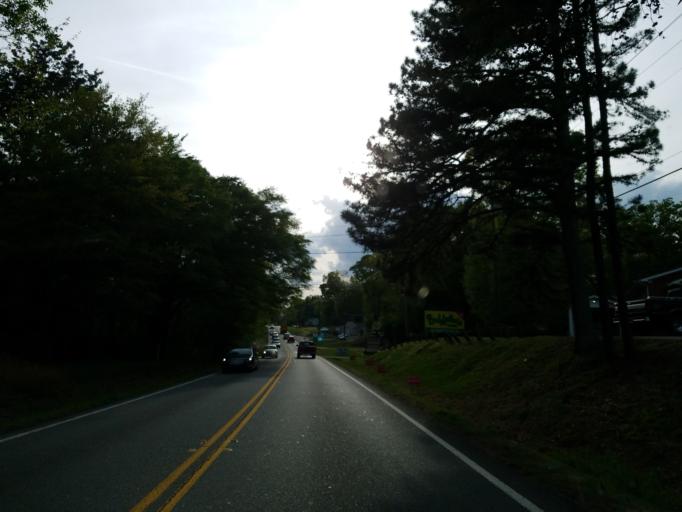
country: US
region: Georgia
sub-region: Cherokee County
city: Canton
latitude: 34.2413
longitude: -84.4208
